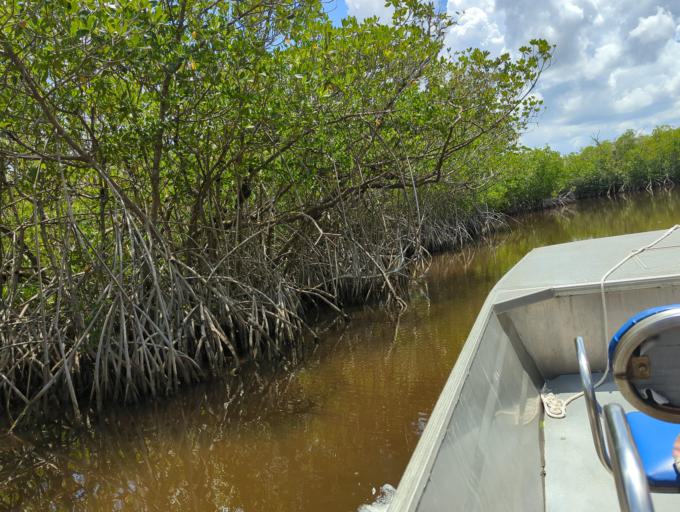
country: US
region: Florida
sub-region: Collier County
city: Marco
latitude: 25.9048
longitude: -81.3749
